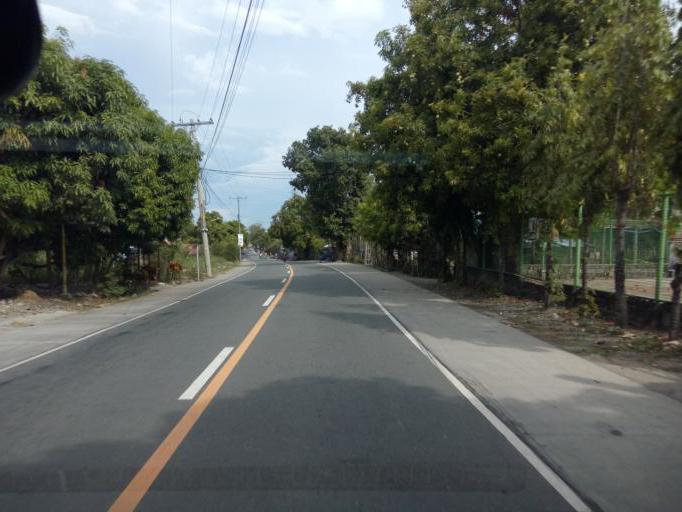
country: PH
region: Central Luzon
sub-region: Province of Nueva Ecija
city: Parista
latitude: 15.8229
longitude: 120.9535
